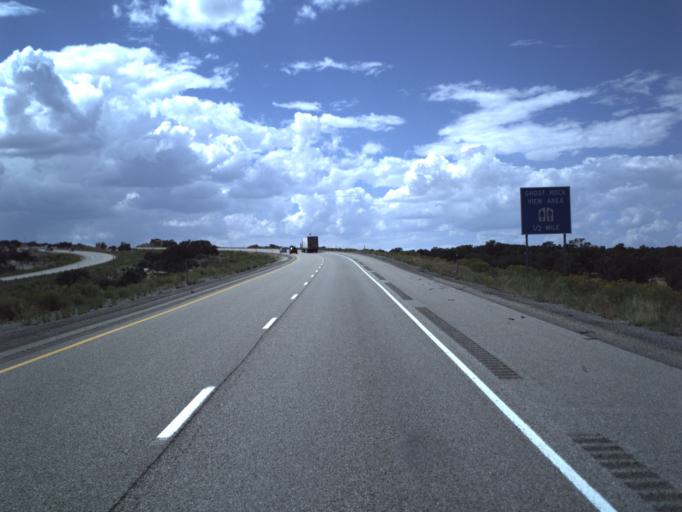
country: US
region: Utah
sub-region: Emery County
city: Ferron
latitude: 38.8660
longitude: -110.8003
